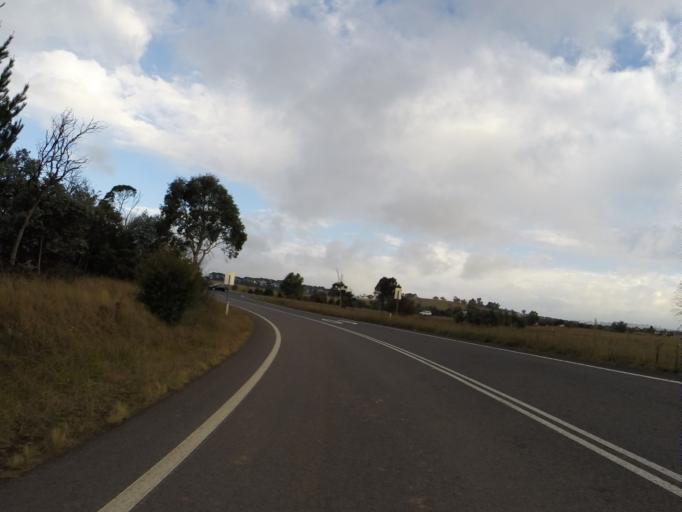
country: AU
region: New South Wales
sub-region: Wingecarribee
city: Moss Vale
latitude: -34.5355
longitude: 150.2804
